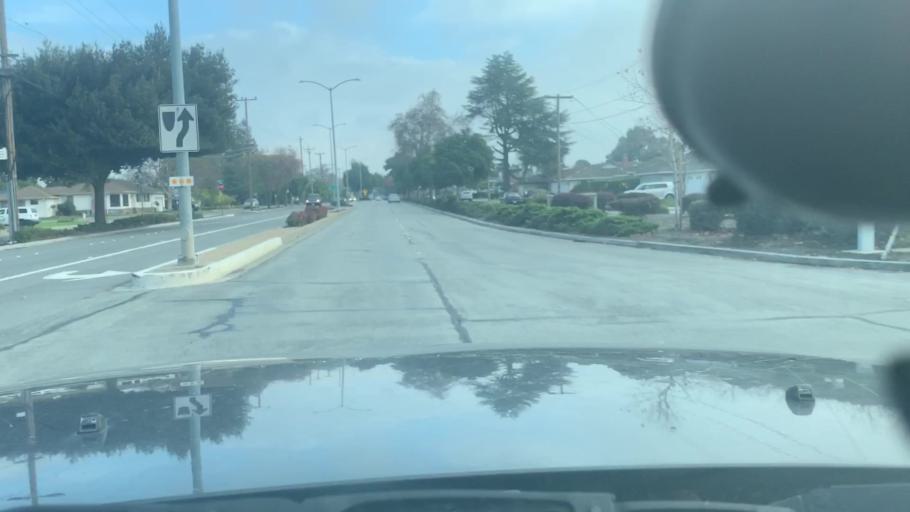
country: US
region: California
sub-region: Alameda County
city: Fremont
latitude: 37.5429
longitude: -122.0112
